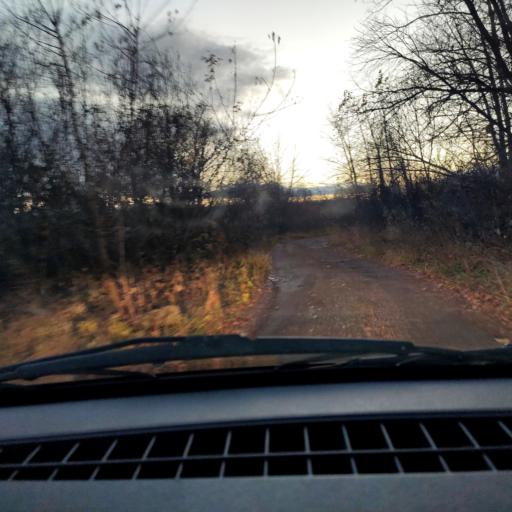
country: RU
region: Bashkortostan
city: Ufa
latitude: 54.6520
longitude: 55.8960
